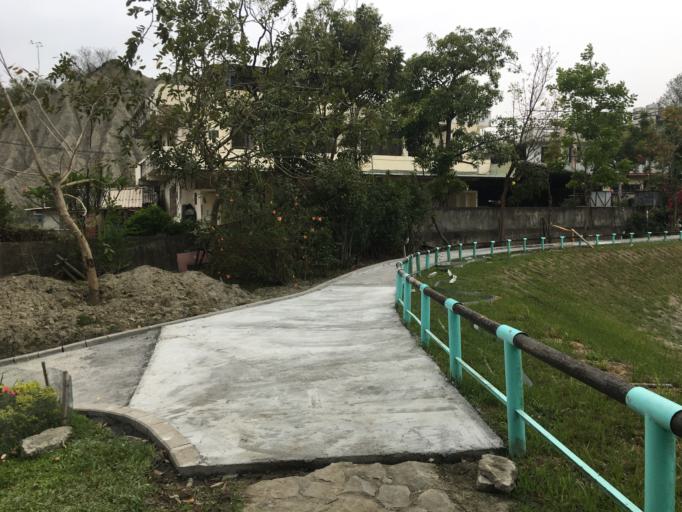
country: TW
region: Taiwan
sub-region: Tainan
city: Tainan
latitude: 22.8858
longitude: 120.3888
